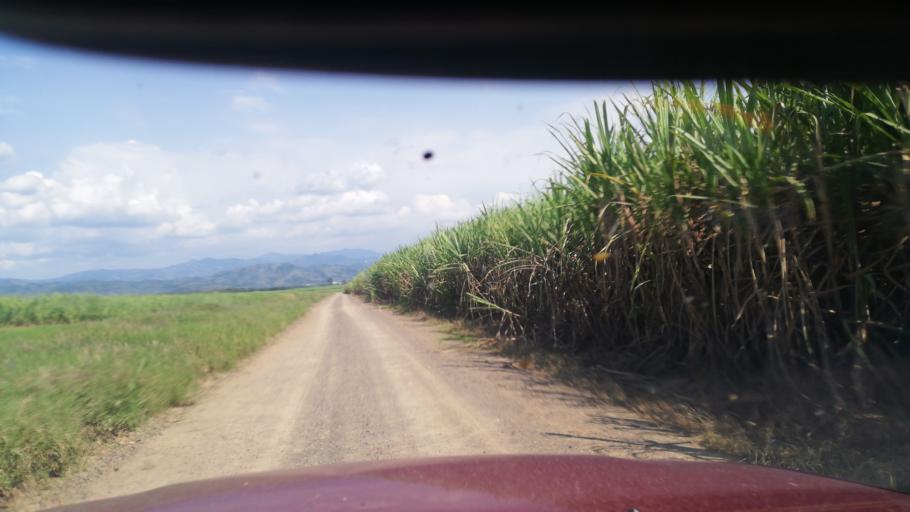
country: CO
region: Risaralda
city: La Virginia
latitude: 4.8923
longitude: -75.9250
